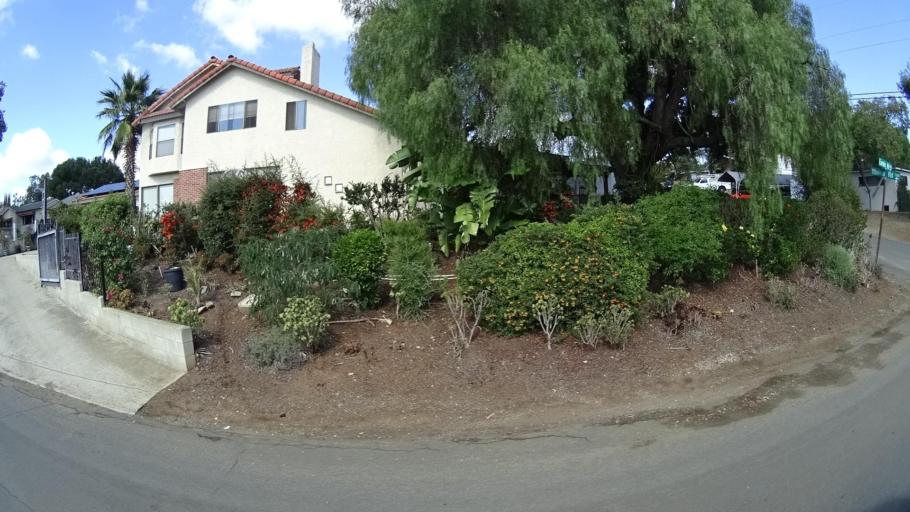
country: US
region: California
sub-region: San Diego County
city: Casa de Oro-Mount Helix
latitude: 32.7383
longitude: -116.9644
